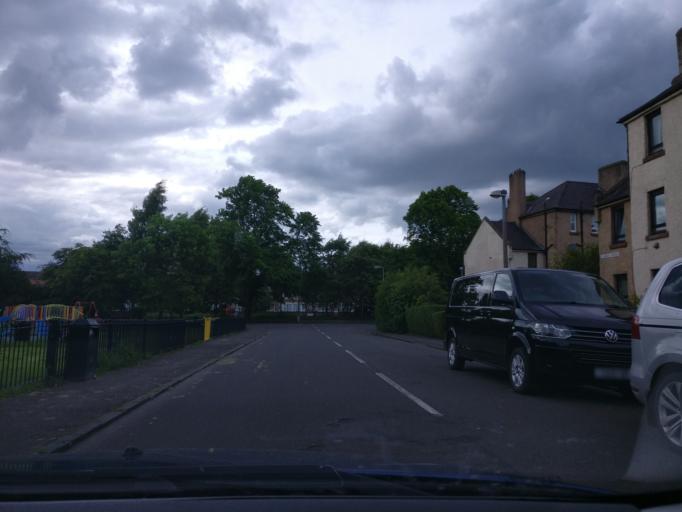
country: GB
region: Scotland
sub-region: West Lothian
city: Seafield
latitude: 55.9587
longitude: -3.1436
